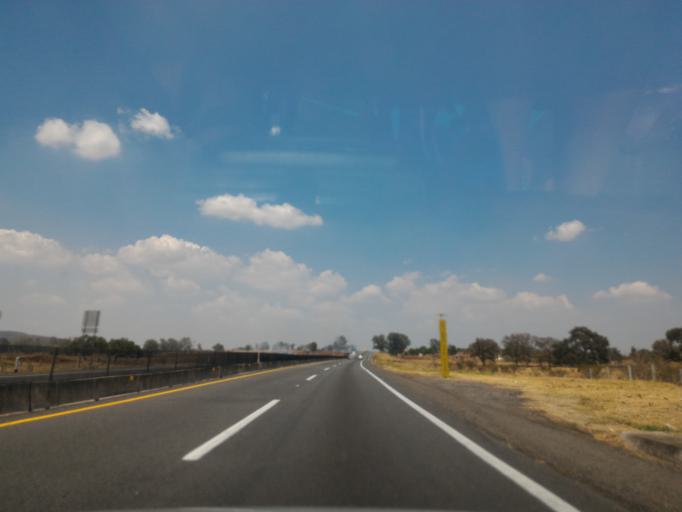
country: MX
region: Jalisco
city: Tepatitlan de Morelos
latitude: 20.8682
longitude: -102.7548
